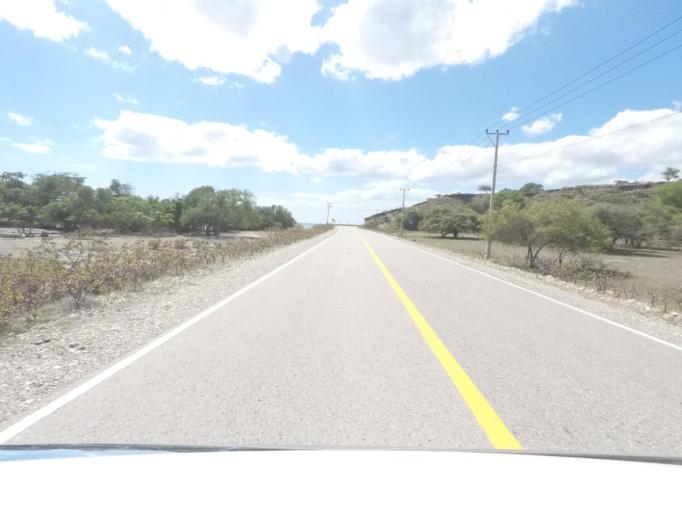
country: TL
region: Baucau
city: Baucau
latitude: -8.4387
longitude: 126.6591
